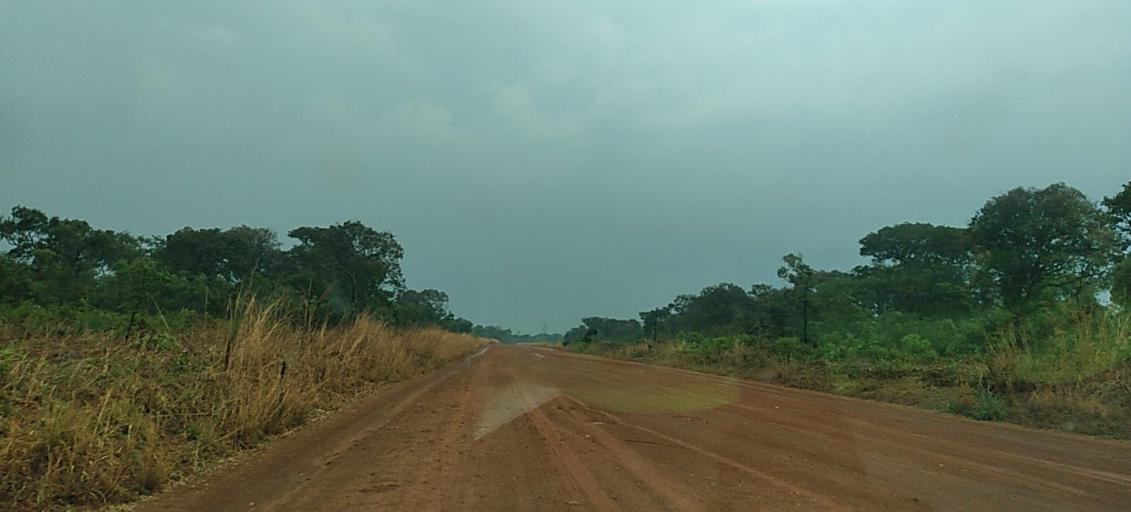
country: ZM
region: North-Western
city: Mwinilunga
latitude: -11.6115
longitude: 24.3985
